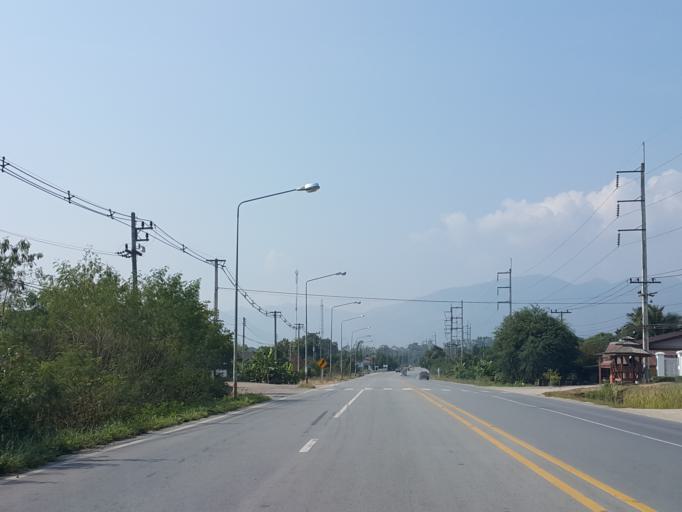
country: TH
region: Chiang Mai
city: Chom Thong
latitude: 18.3091
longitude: 98.6522
